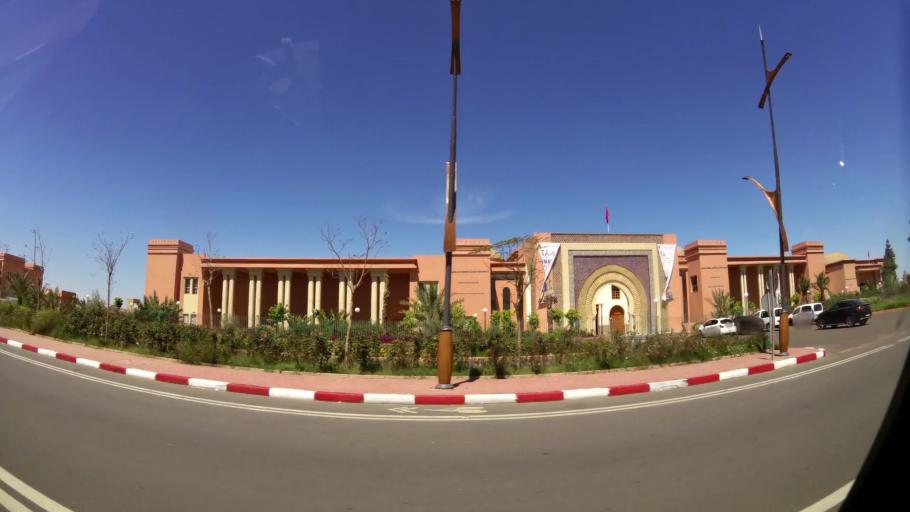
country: MA
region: Marrakech-Tensift-Al Haouz
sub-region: Marrakech
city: Marrakesh
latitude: 31.6122
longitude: -7.9939
